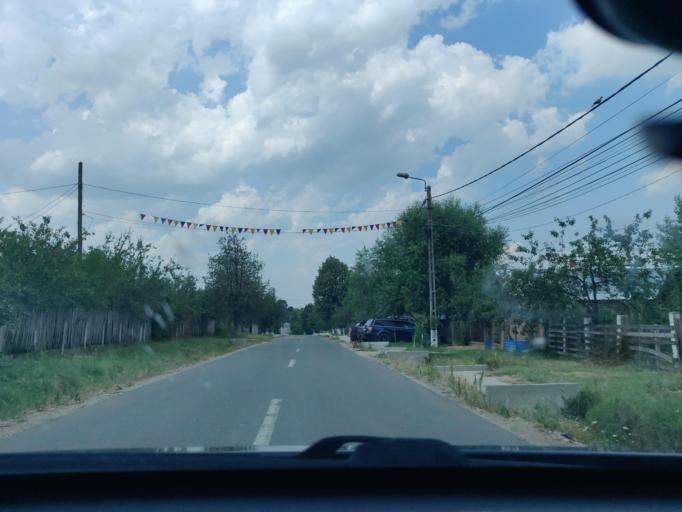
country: RO
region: Teleorman
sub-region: Comuna Sarbeni
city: Sarbeni
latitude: 44.4712
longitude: 25.3869
